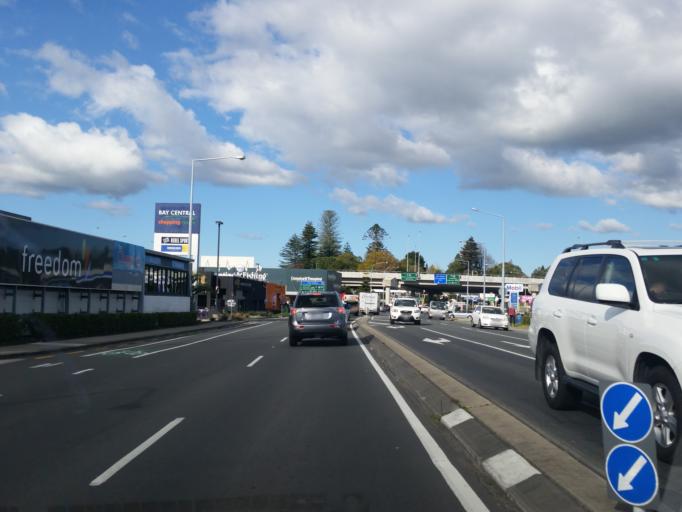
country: NZ
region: Bay of Plenty
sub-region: Tauranga City
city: Tauranga
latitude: -37.6740
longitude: 176.1647
